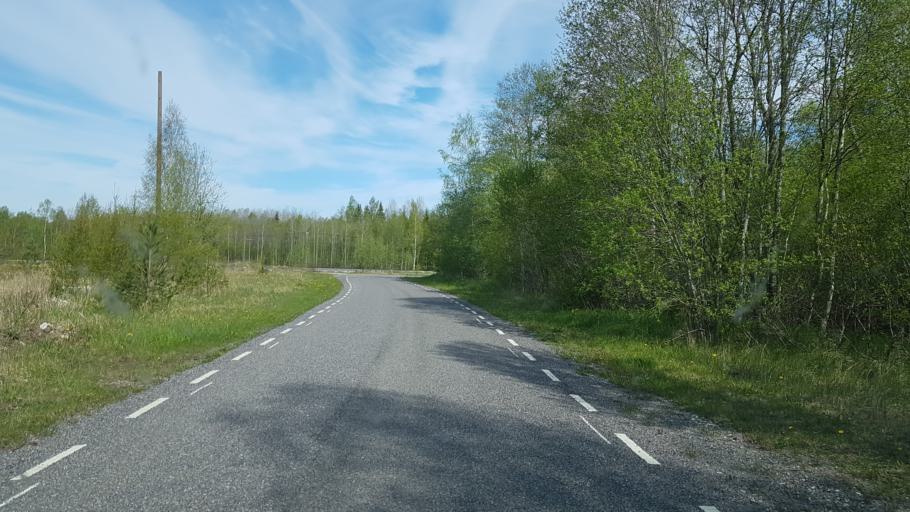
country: EE
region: Ida-Virumaa
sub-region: Kohtla-Nomme vald
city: Kohtla-Nomme
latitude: 59.3597
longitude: 27.1711
